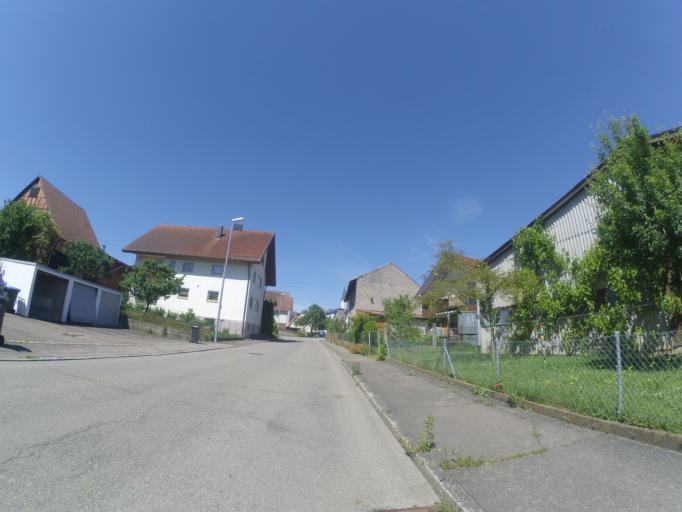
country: DE
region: Baden-Wuerttemberg
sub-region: Tuebingen Region
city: Dornstadt
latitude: 48.4822
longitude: 9.9127
